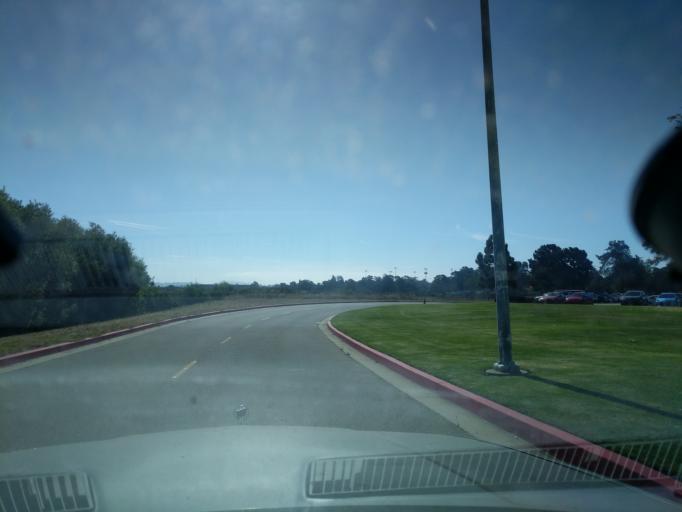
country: US
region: California
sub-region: Santa Barbara County
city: Isla Vista
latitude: 34.4234
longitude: -119.8627
